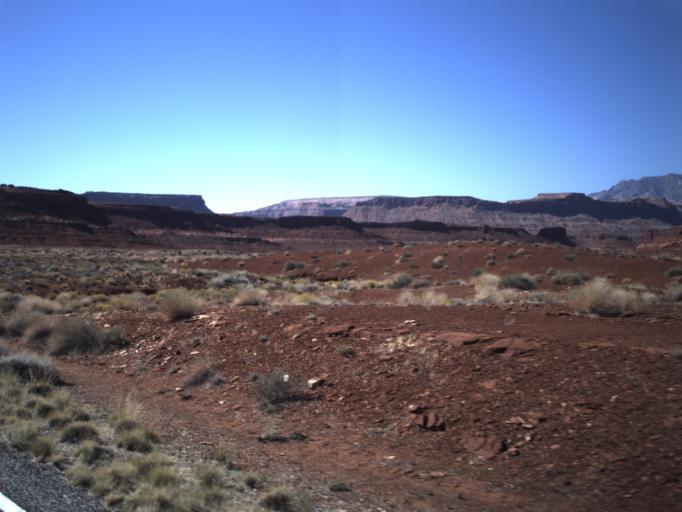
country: US
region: Utah
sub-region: San Juan County
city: Blanding
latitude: 37.8361
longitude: -110.3570
